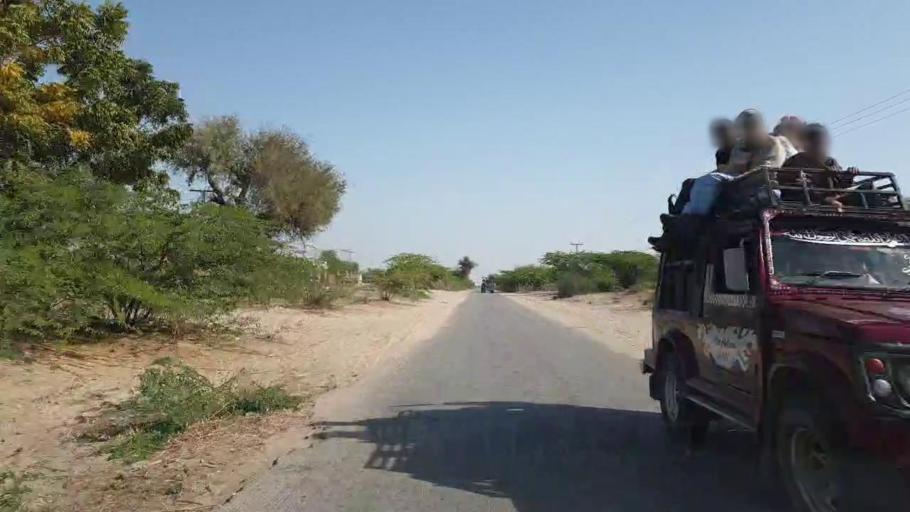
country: PK
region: Sindh
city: Chor
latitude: 25.4521
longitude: 69.7574
